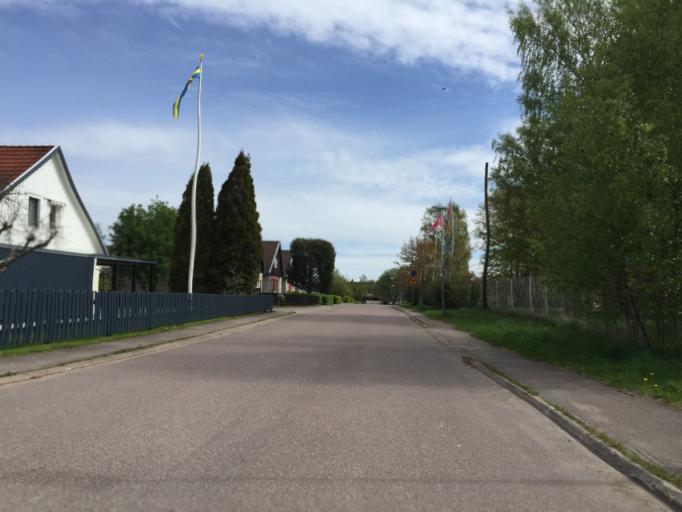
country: SE
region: Dalarna
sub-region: Ludvika Kommun
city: Ludvika
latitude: 60.1261
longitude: 15.1753
